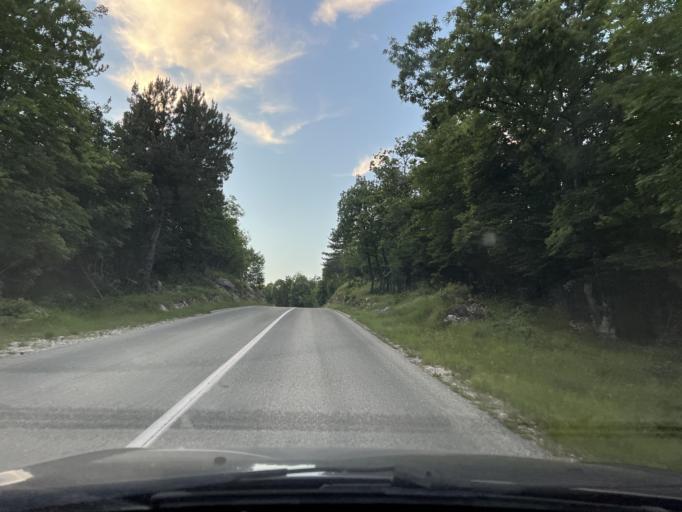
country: HR
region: Primorsko-Goranska
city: Klana
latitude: 45.4488
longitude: 14.3234
